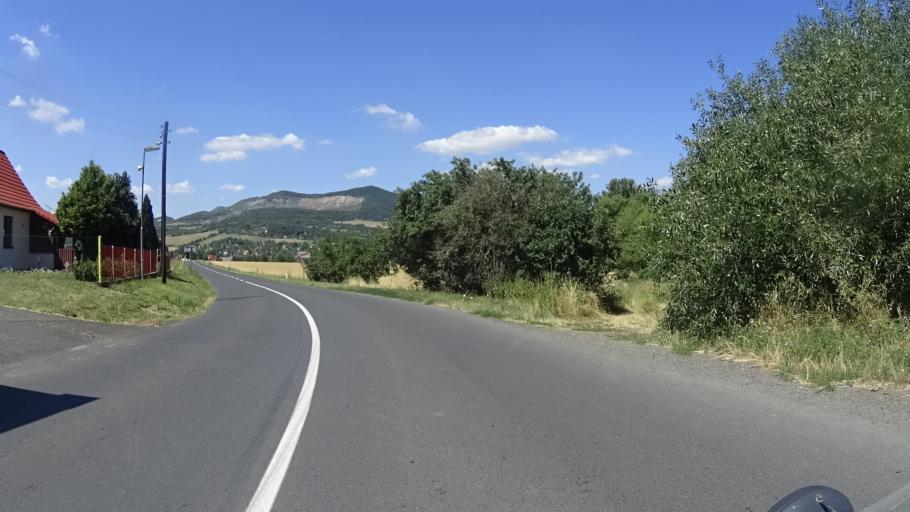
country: CZ
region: Ustecky
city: Lovosice
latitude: 50.5678
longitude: 14.0553
